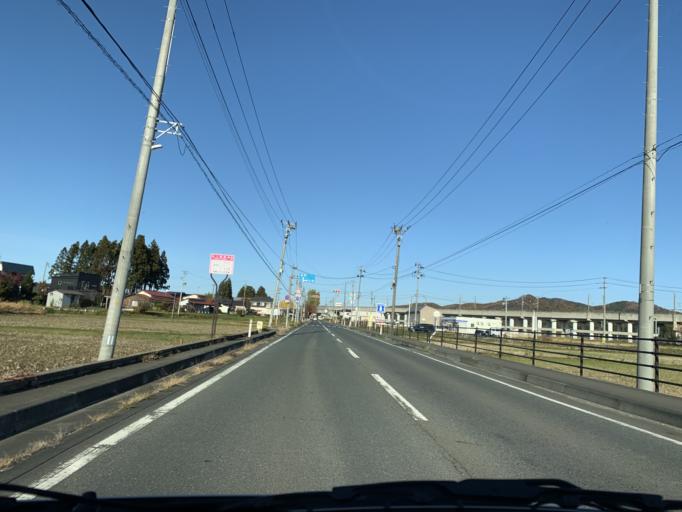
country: JP
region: Iwate
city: Kitakami
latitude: 39.2540
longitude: 141.1093
